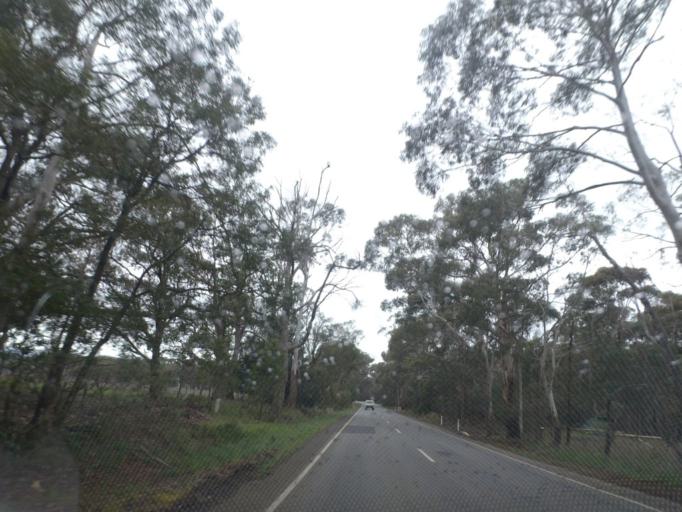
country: AU
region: Victoria
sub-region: Hume
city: Sunbury
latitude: -37.3449
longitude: 144.6830
